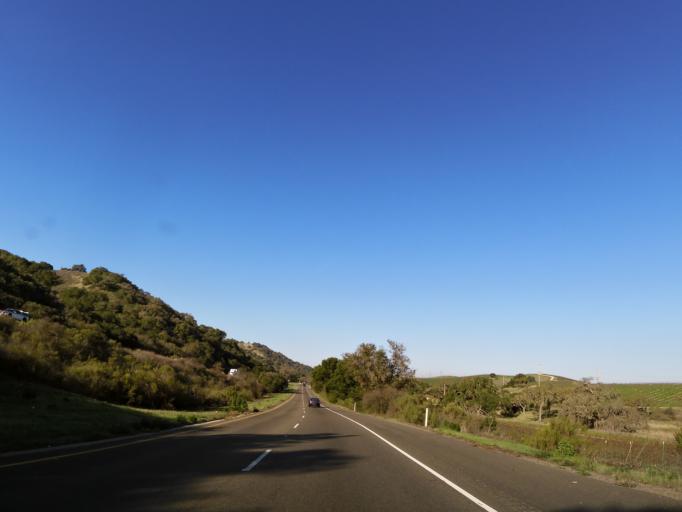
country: US
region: California
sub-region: Santa Barbara County
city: Los Alamos
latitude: 34.7167
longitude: -120.1940
